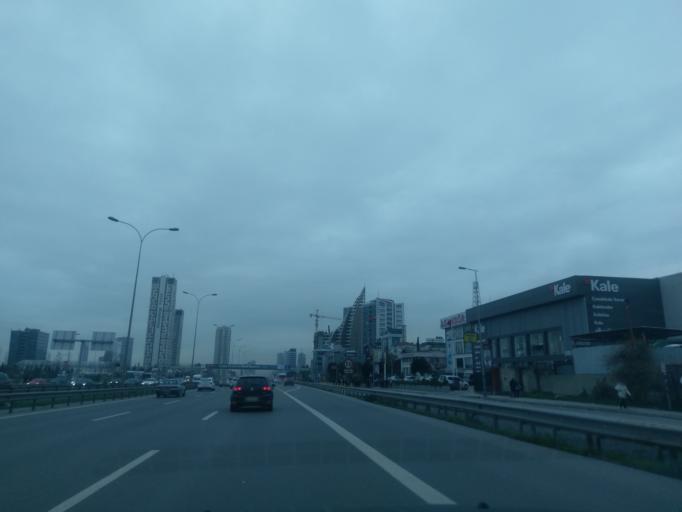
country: TR
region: Istanbul
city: Maltepe
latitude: 40.9081
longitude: 29.2069
